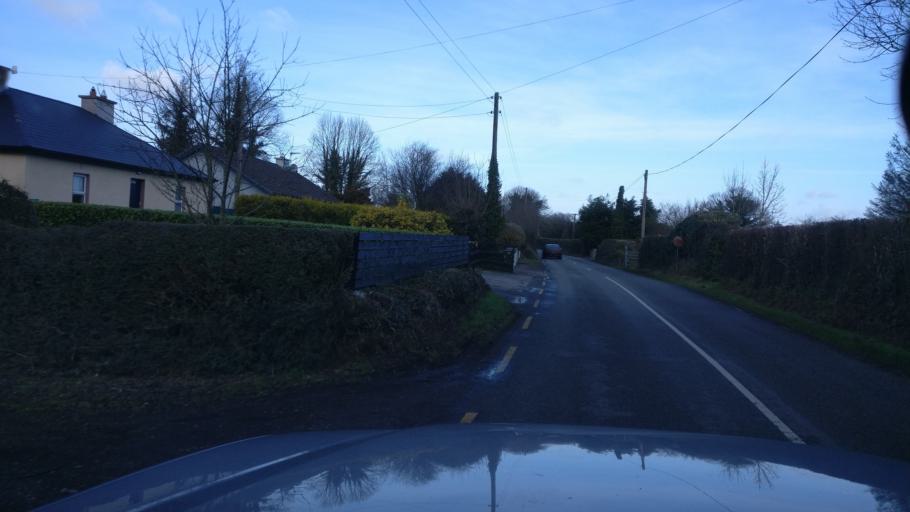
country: IE
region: Leinster
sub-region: Kilkenny
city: Castlecomer
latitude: 52.8463
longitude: -7.1790
